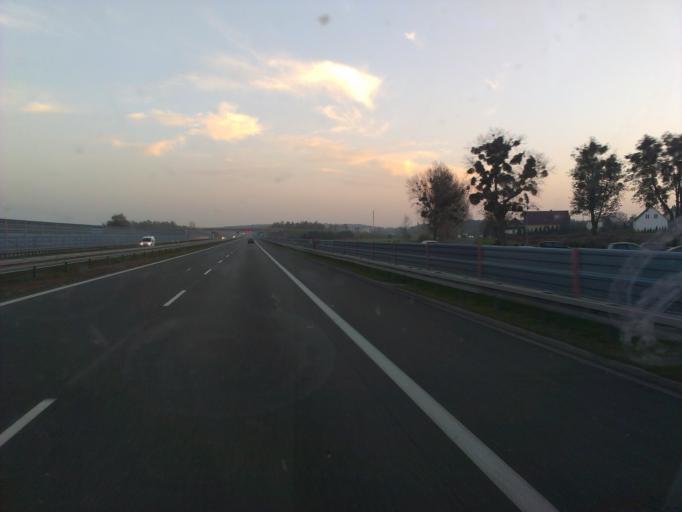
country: PL
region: Opole Voivodeship
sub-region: Powiat krapkowicki
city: Krapkowice
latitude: 50.5073
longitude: 17.9665
